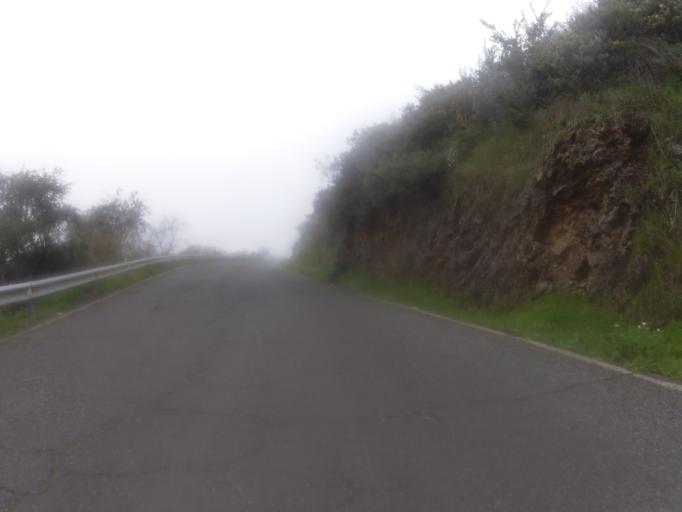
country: ES
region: Canary Islands
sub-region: Provincia de Las Palmas
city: Vega de San Mateo
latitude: 27.9860
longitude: -15.5688
